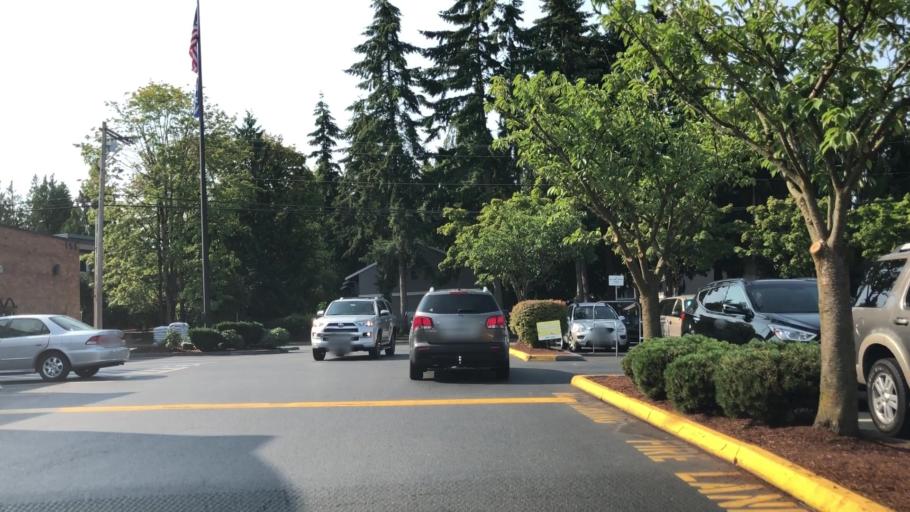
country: US
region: Washington
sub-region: Snohomish County
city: Alderwood Manor
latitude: 47.8396
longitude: -122.2974
